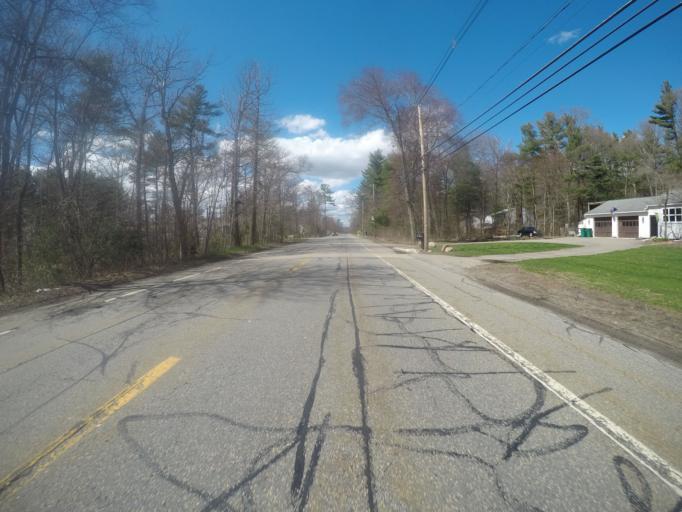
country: US
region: Massachusetts
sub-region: Bristol County
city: Easton
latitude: 42.0287
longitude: -71.0697
